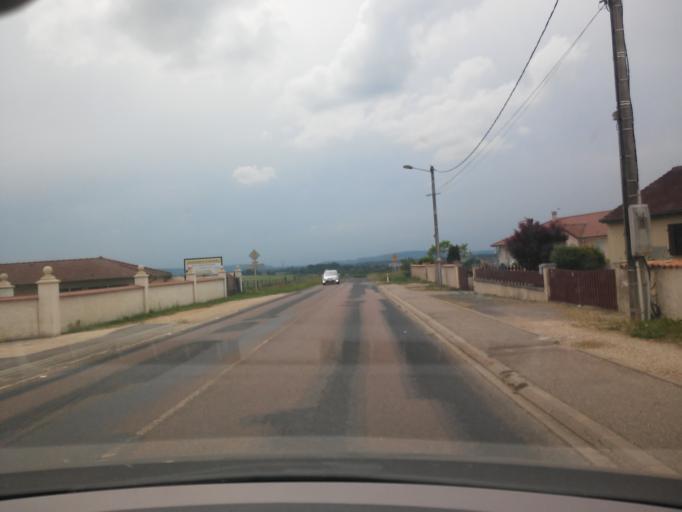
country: FR
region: Lorraine
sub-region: Departement de la Meuse
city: Vigneulles-les-Hattonchatel
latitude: 48.8429
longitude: 5.7521
